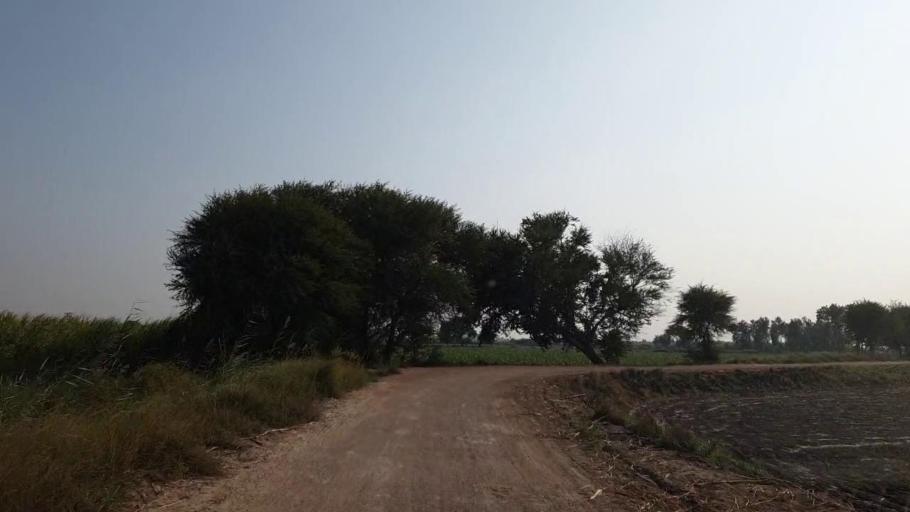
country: PK
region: Sindh
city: Bulri
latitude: 24.9741
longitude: 68.3778
